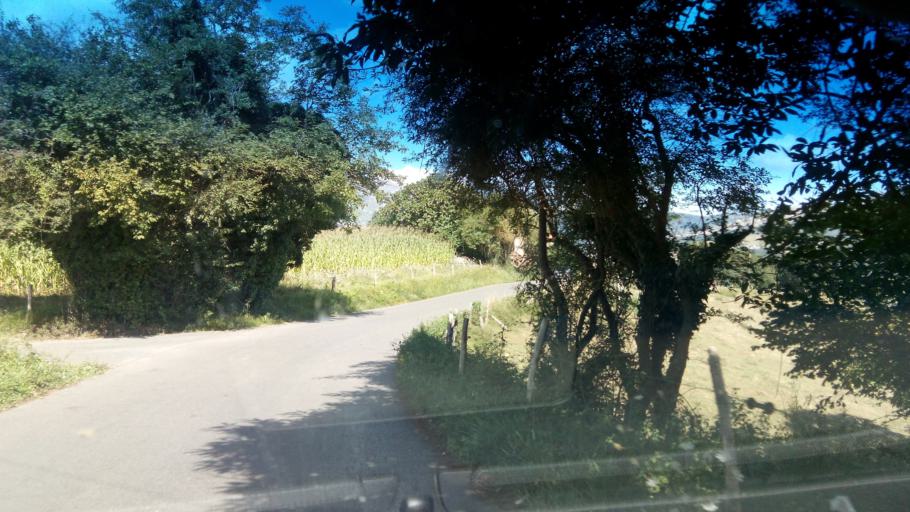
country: ES
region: Asturias
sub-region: Province of Asturias
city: Parres
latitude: 43.3775
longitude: -5.1768
